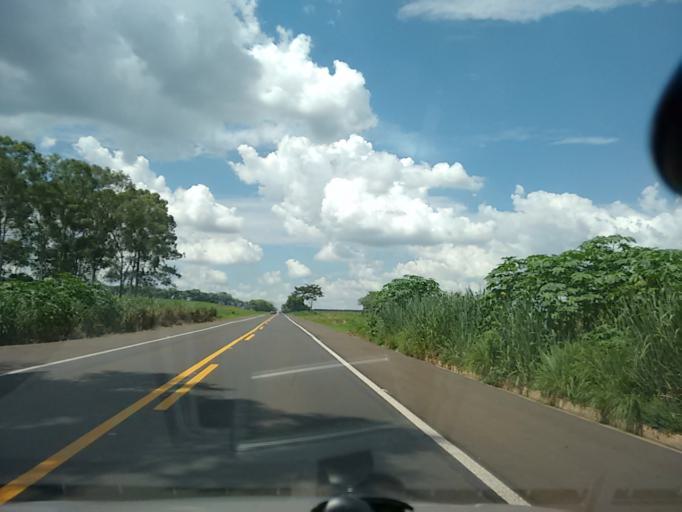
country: BR
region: Sao Paulo
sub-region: Osvaldo Cruz
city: Osvaldo Cruz
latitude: -21.8801
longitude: -50.8636
